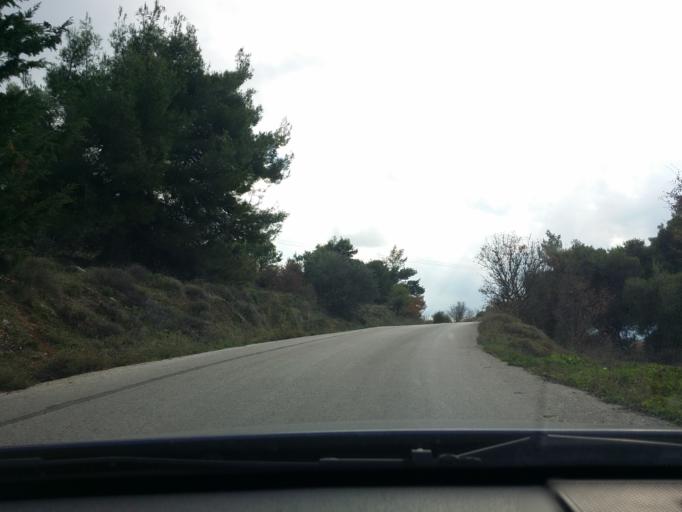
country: GR
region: Attica
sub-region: Nomarchia Anatolikis Attikis
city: Varnavas
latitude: 38.2258
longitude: 23.9270
